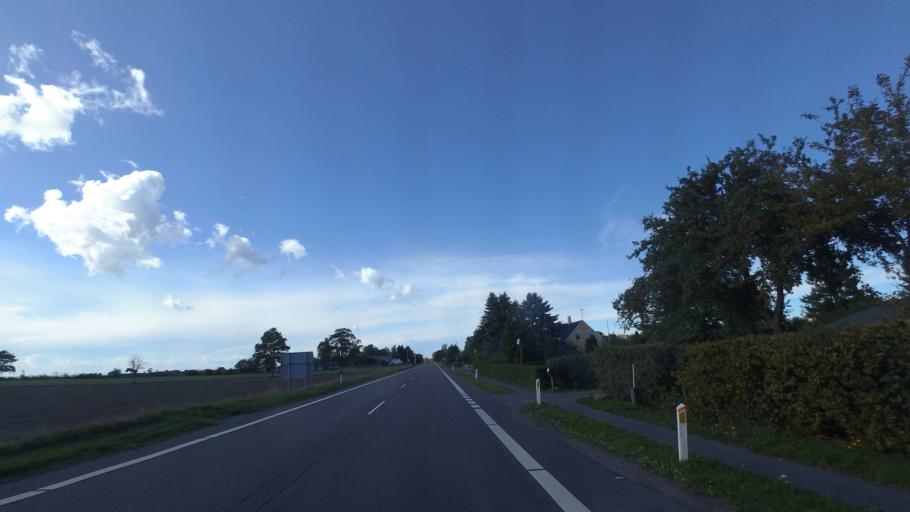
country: DK
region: Capital Region
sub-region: Bornholm Kommune
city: Ronne
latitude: 55.0716
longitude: 14.8082
